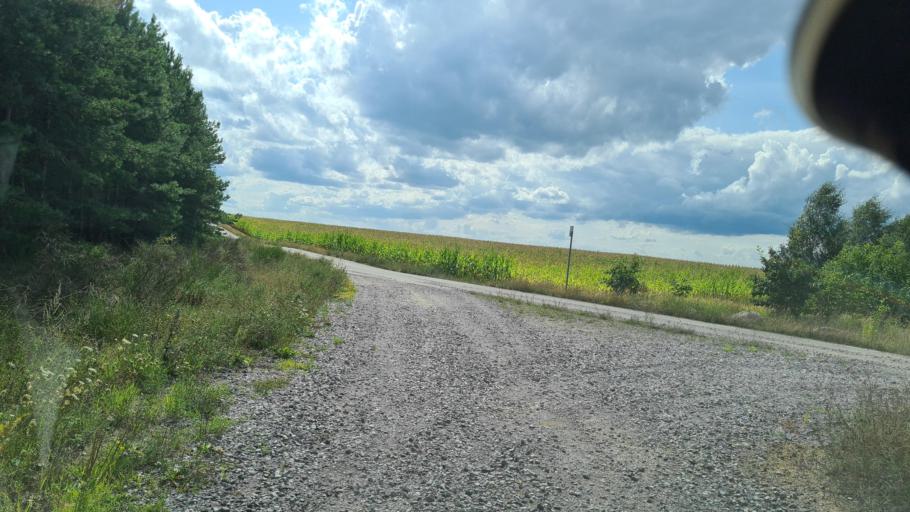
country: DE
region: Brandenburg
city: Drebkau
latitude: 51.6035
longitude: 14.2920
